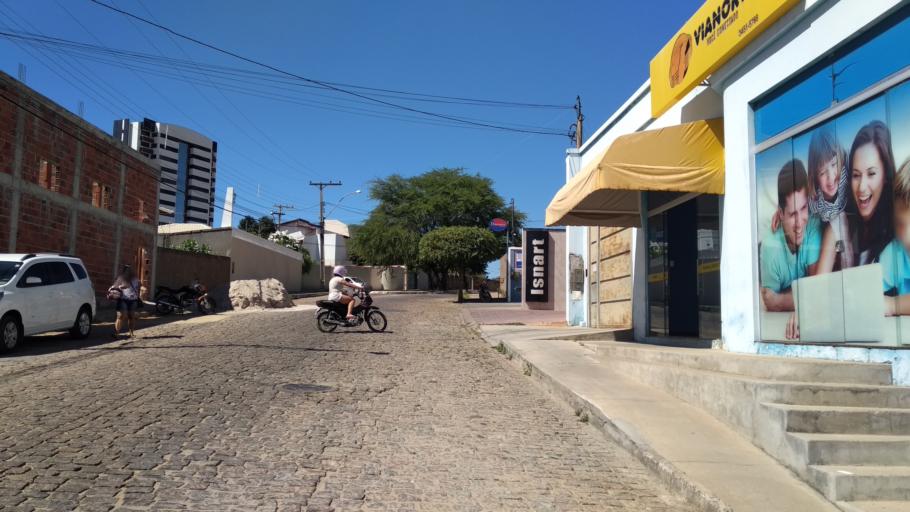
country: BR
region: Bahia
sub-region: Guanambi
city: Guanambi
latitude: -14.2283
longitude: -42.7772
